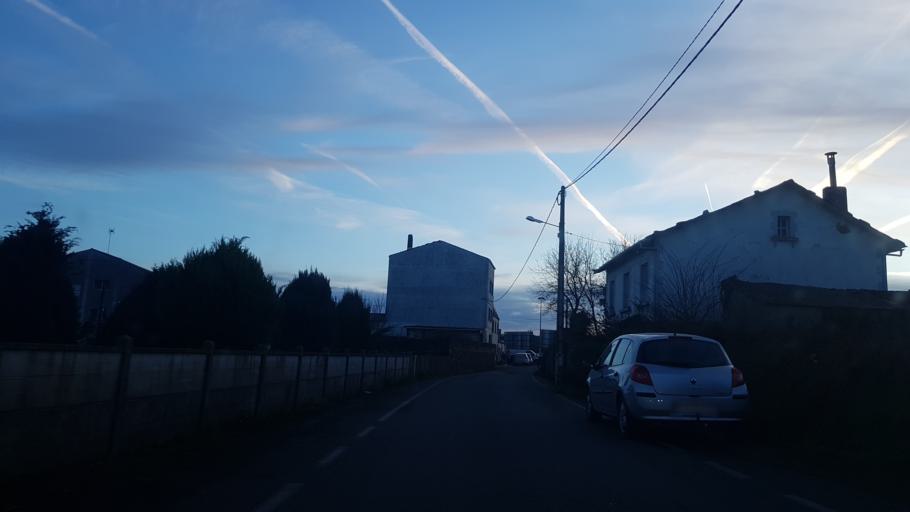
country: ES
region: Galicia
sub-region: Provincia de Lugo
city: Lugo
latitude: 43.0337
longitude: -7.5628
